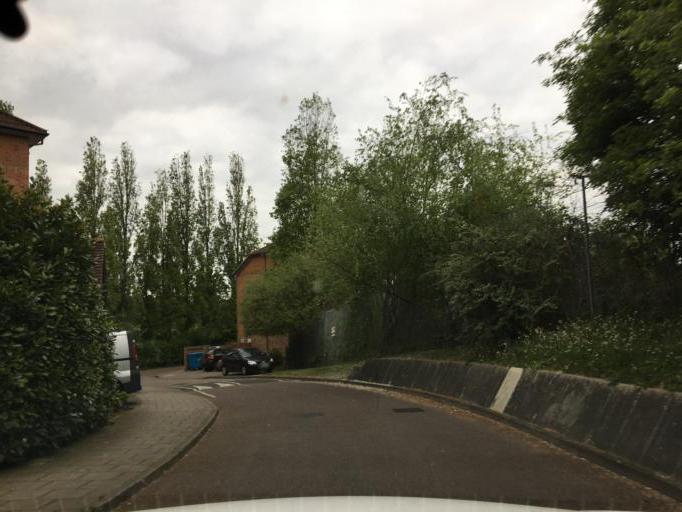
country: GB
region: England
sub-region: Greater London
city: Blackheath
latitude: 51.4380
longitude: 0.0123
